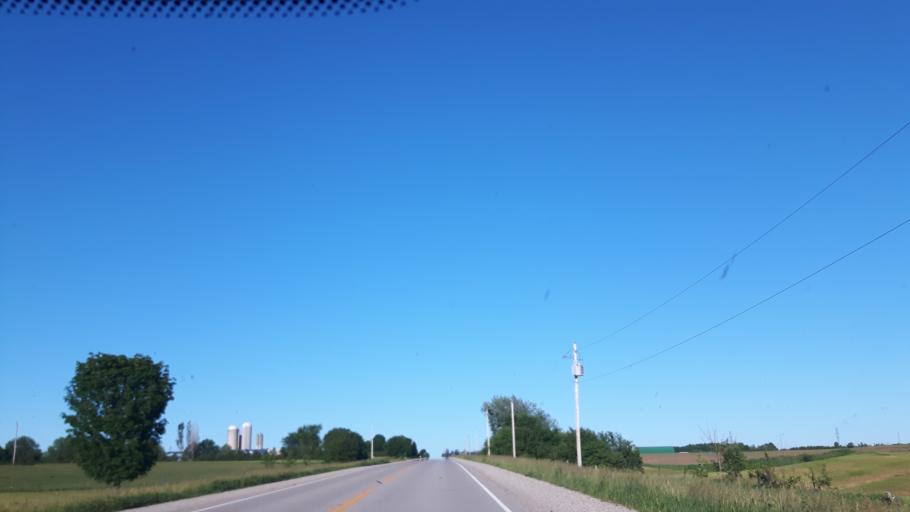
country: CA
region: Ontario
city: Goderich
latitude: 43.6428
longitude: -81.6582
